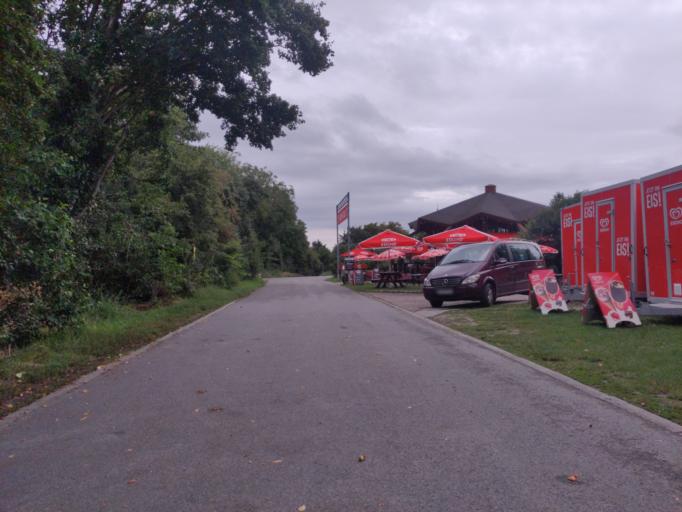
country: AT
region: Vienna
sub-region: Wien Stadt
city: Vienna
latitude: 48.2499
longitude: 16.3859
